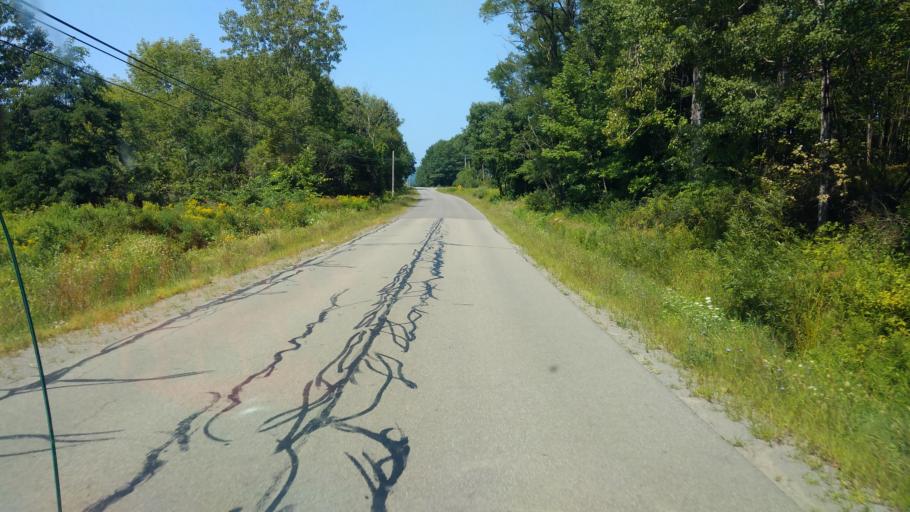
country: US
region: New York
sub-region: Allegany County
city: Belmont
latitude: 42.3115
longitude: -78.0639
